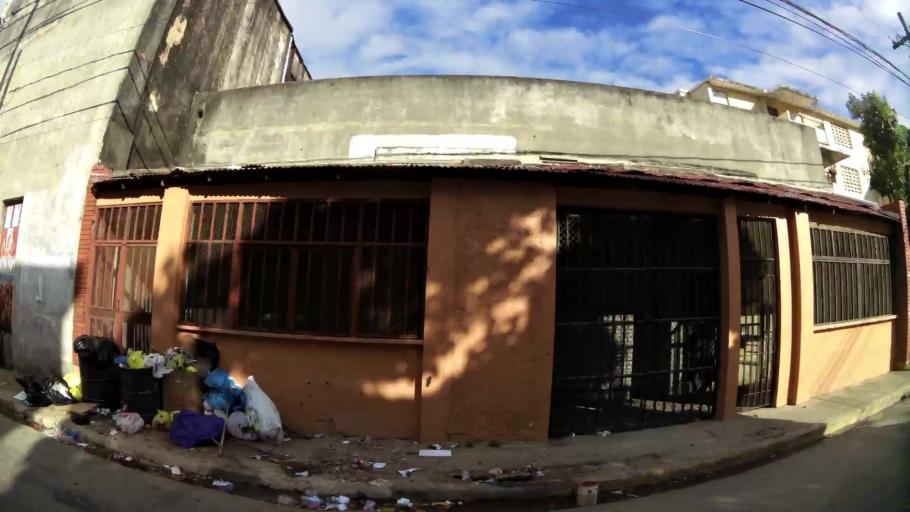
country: DO
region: Nacional
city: San Carlos
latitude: 18.4751
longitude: -69.8895
